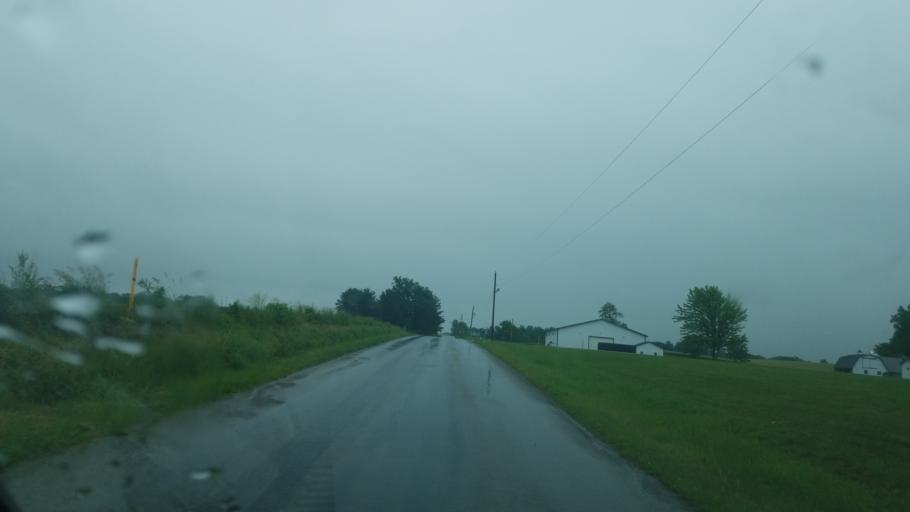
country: US
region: Ohio
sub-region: Huron County
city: Plymouth
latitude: 40.9839
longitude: -82.5946
